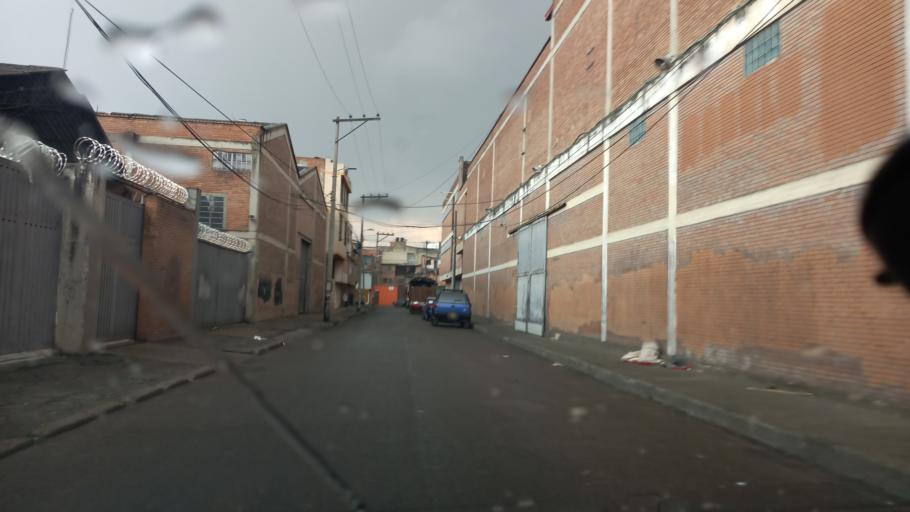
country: CO
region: Cundinamarca
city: Funza
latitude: 4.6708
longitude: -74.1422
